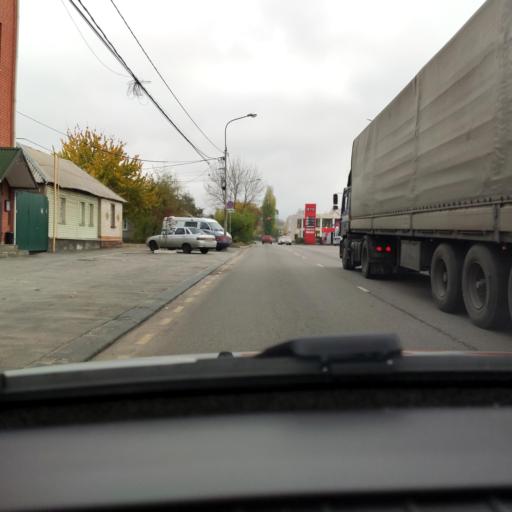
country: RU
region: Voronezj
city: Voronezh
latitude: 51.6654
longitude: 39.1752
